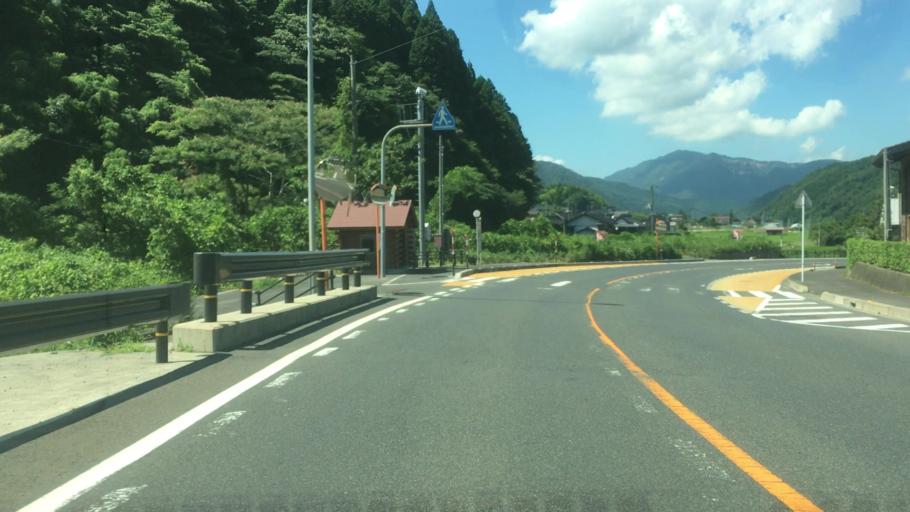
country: JP
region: Tottori
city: Tottori
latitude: 35.2456
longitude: 134.2286
